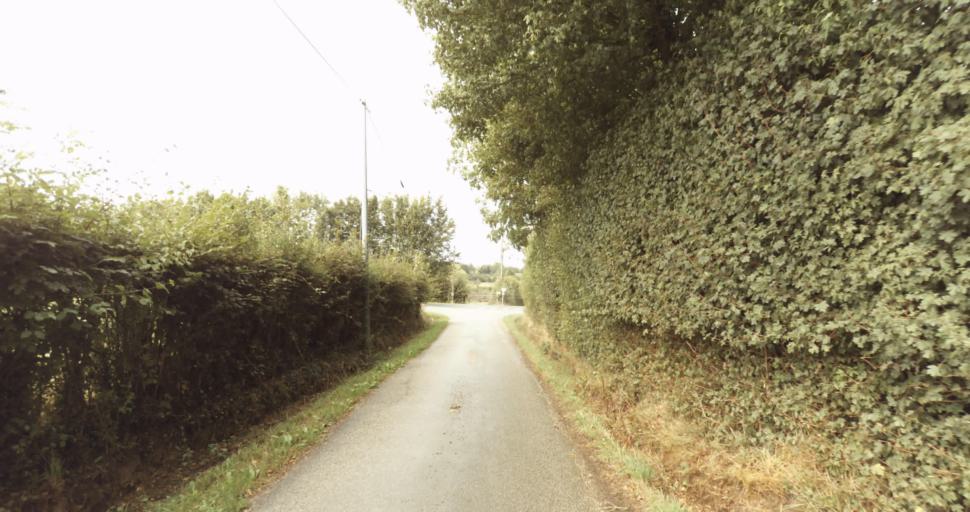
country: FR
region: Lower Normandy
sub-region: Departement de l'Orne
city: Sainte-Gauburge-Sainte-Colombe
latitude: 48.7127
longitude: 0.4155
